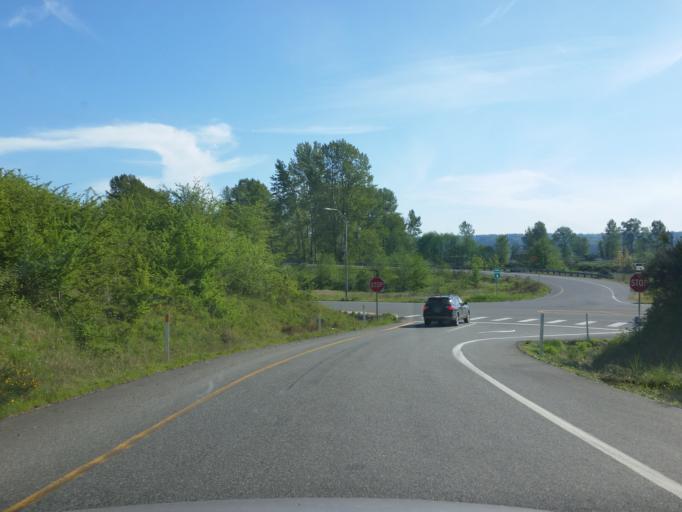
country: US
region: Washington
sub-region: Snohomish County
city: Snohomish
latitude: 47.9167
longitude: -122.1090
